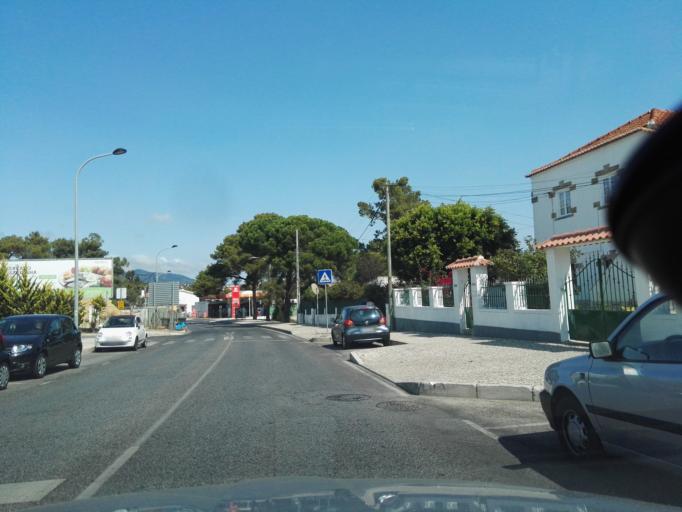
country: PT
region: Lisbon
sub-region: Cascais
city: Estoril
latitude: 38.7101
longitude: -9.3862
